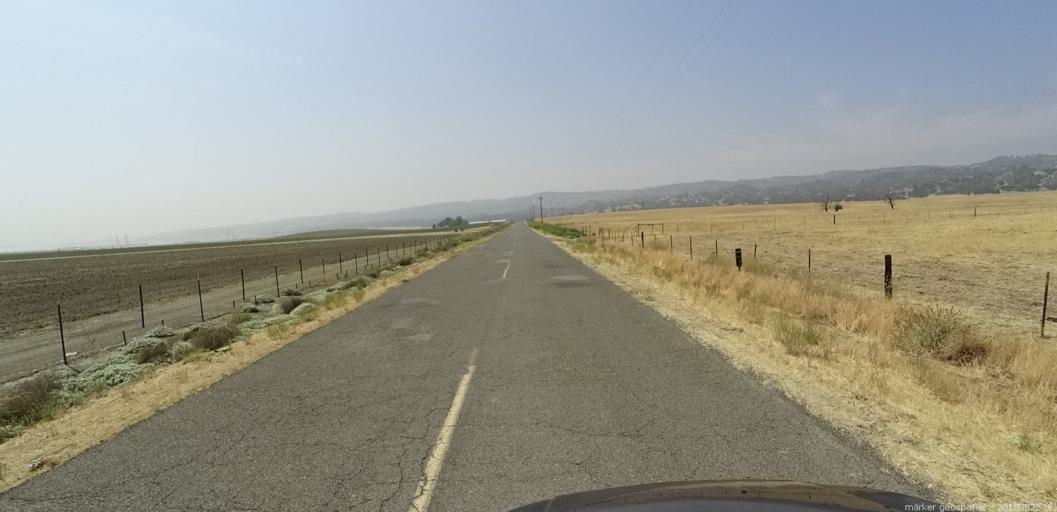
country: US
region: California
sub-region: San Luis Obispo County
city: Shandon
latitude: 35.8412
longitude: -120.3809
